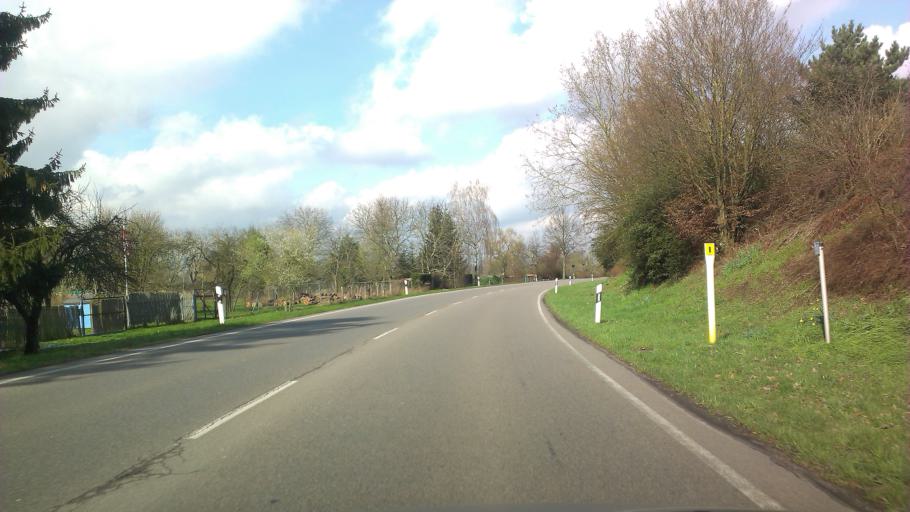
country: DE
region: Baden-Wuerttemberg
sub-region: Karlsruhe Region
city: Eppelheim
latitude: 49.3783
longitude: 8.6566
